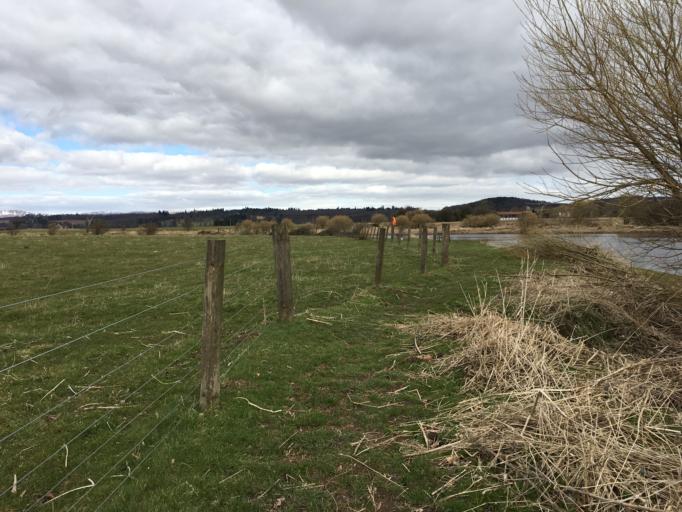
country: GB
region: Scotland
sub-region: Stirling
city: Bridge of Allan
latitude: 56.1400
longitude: -3.9754
